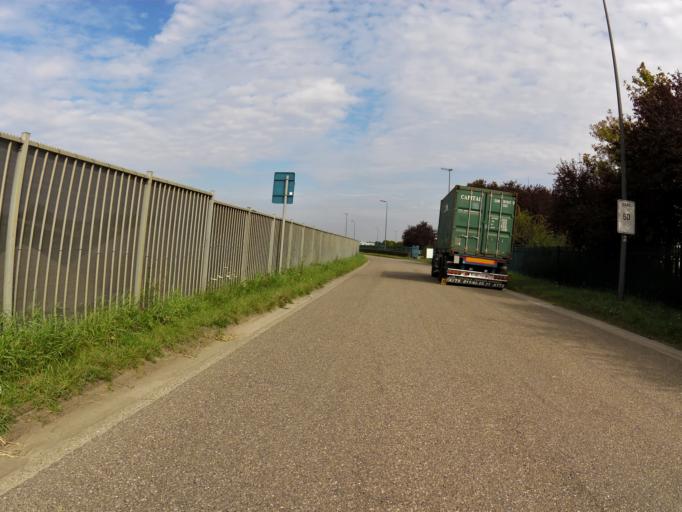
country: BE
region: Flanders
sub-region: Provincie Limburg
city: Lanaken
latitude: 50.8788
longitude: 5.6468
